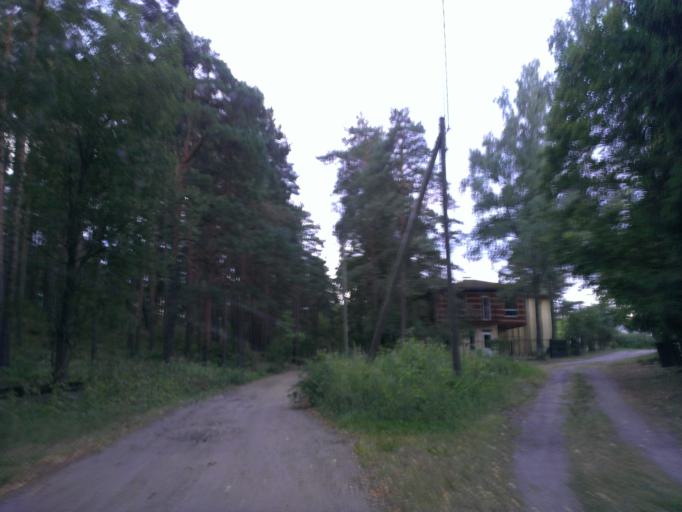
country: LV
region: Riga
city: Bergi
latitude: 56.9822
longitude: 24.3066
